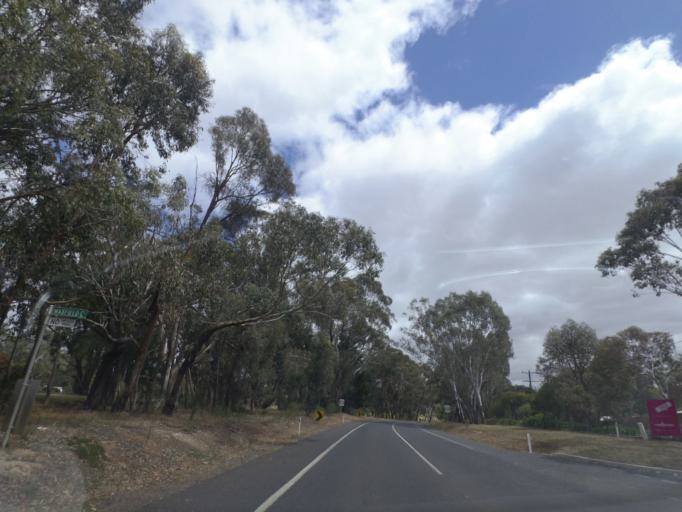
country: AU
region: Victoria
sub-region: Whittlesea
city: Whittlesea
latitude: -37.2136
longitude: 145.0499
